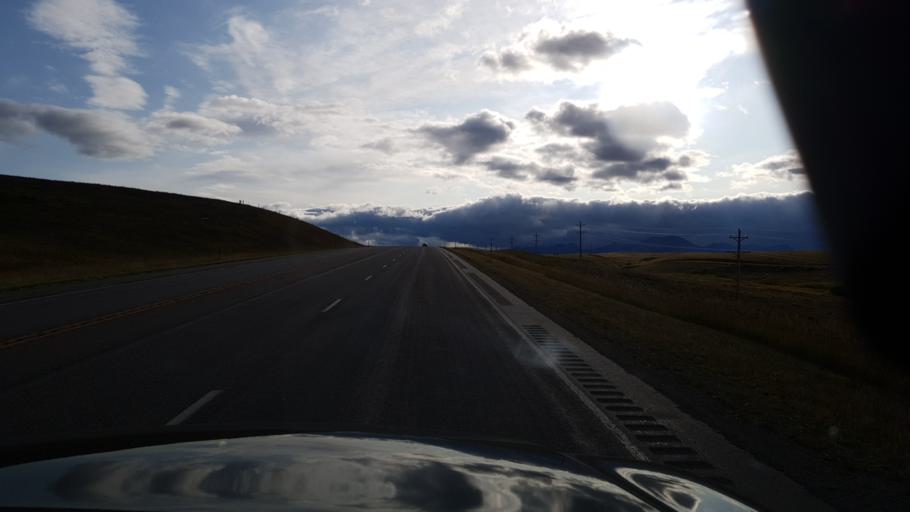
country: US
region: Montana
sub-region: Glacier County
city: South Browning
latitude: 48.5142
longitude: -113.0875
